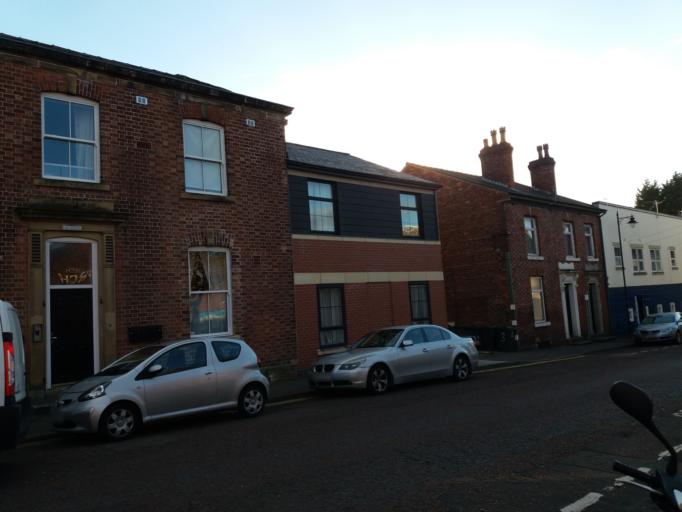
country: GB
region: England
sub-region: Lancashire
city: Chorley
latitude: 53.6521
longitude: -2.6312
